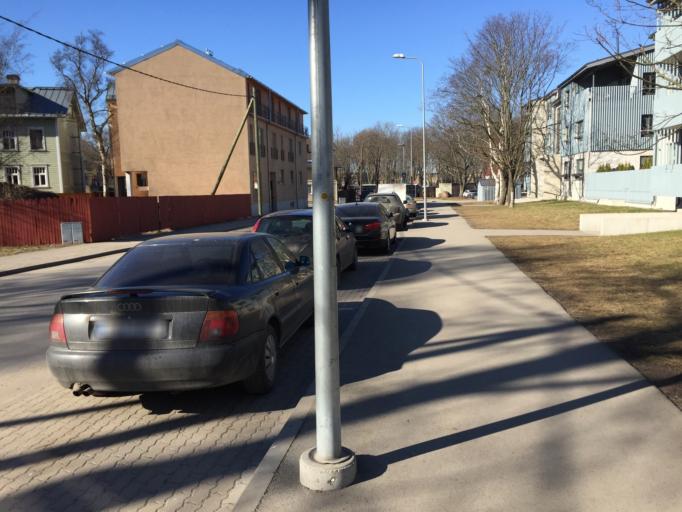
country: EE
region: Harju
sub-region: Tallinna linn
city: Tallinn
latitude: 59.4485
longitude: 24.7342
